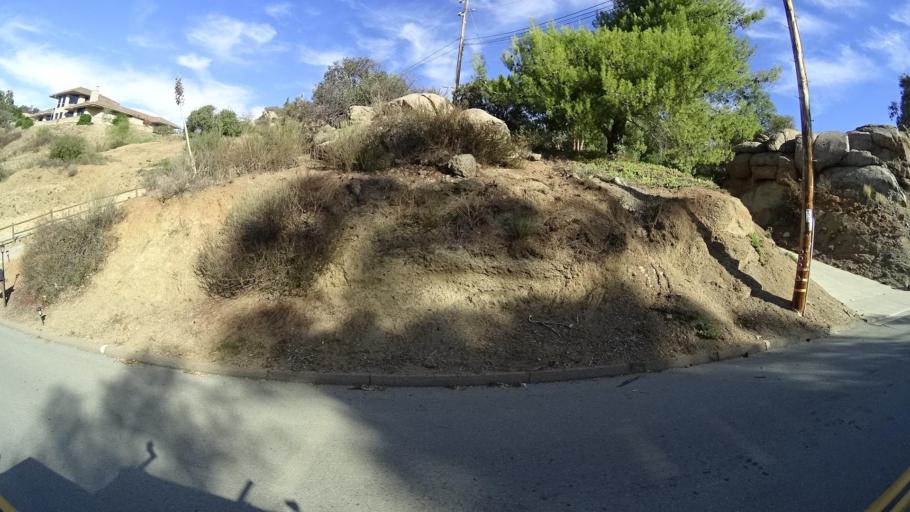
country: US
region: California
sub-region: San Diego County
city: Alpine
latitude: 32.8142
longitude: -116.7250
